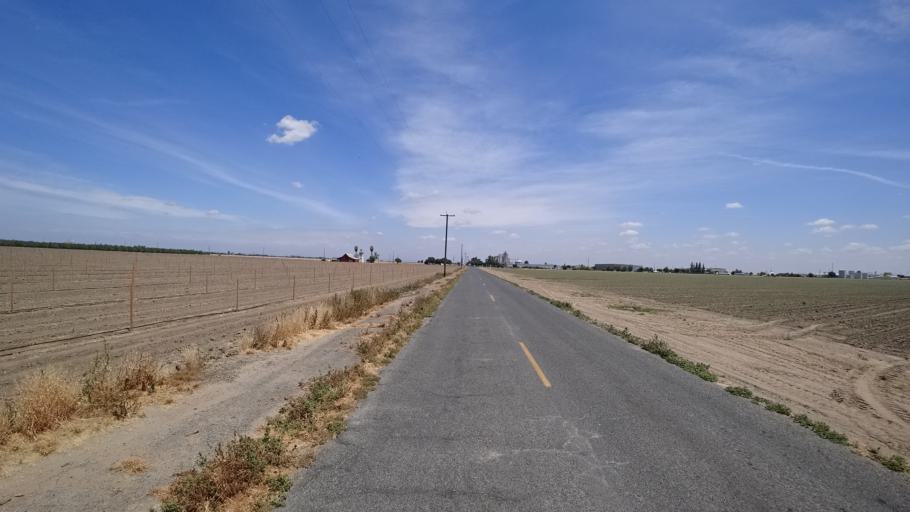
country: US
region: California
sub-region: Kings County
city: Home Garden
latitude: 36.2838
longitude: -119.6607
